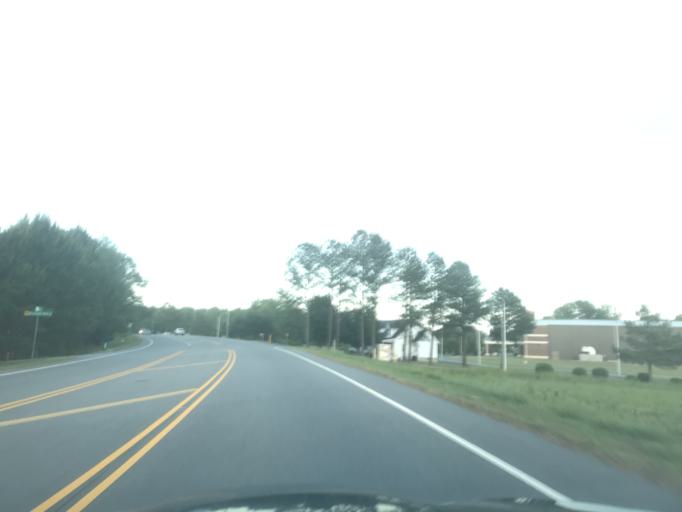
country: US
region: North Carolina
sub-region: Wake County
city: Wendell
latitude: 35.7694
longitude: -78.4110
